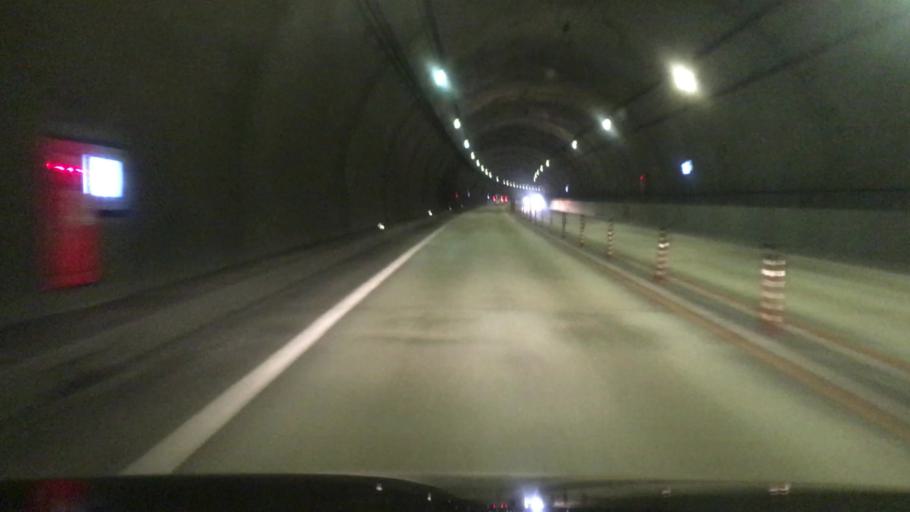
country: JP
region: Hyogo
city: Toyooka
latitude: 35.3660
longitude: 134.7583
